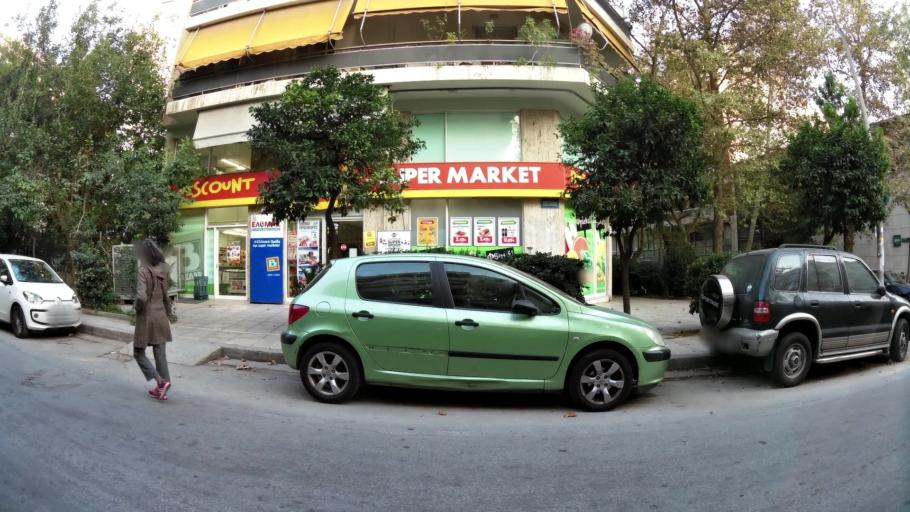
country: GR
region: Attica
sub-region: Nomarchia Athinas
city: Neo Psychiko
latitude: 37.9940
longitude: 23.7689
